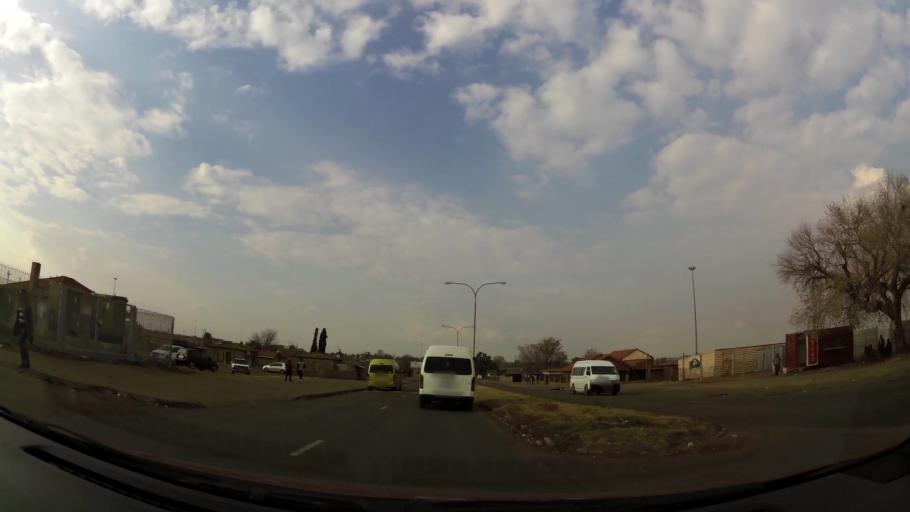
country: ZA
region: Gauteng
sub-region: Sedibeng District Municipality
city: Vereeniging
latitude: -26.6804
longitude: 27.8839
